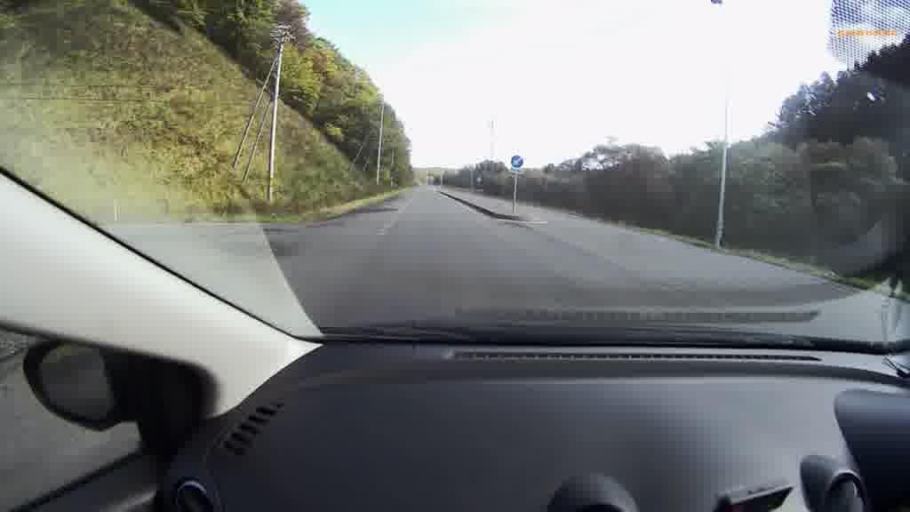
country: JP
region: Hokkaido
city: Kushiro
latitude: 43.0082
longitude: 144.5103
